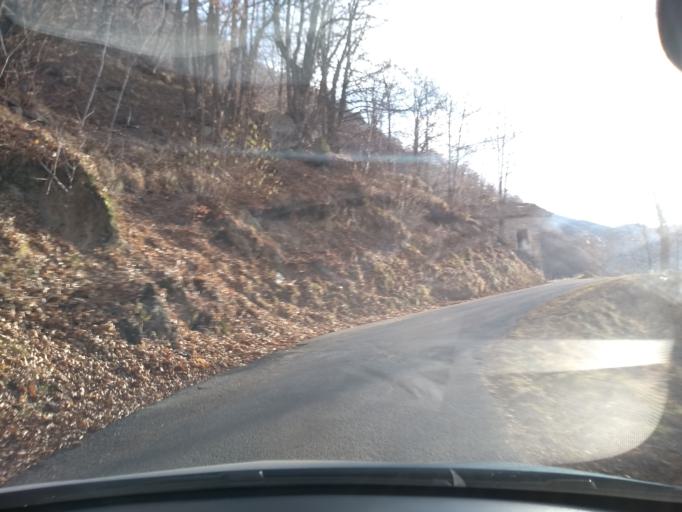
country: IT
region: Piedmont
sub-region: Provincia di Torino
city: Cantoira
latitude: 45.3475
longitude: 7.3815
